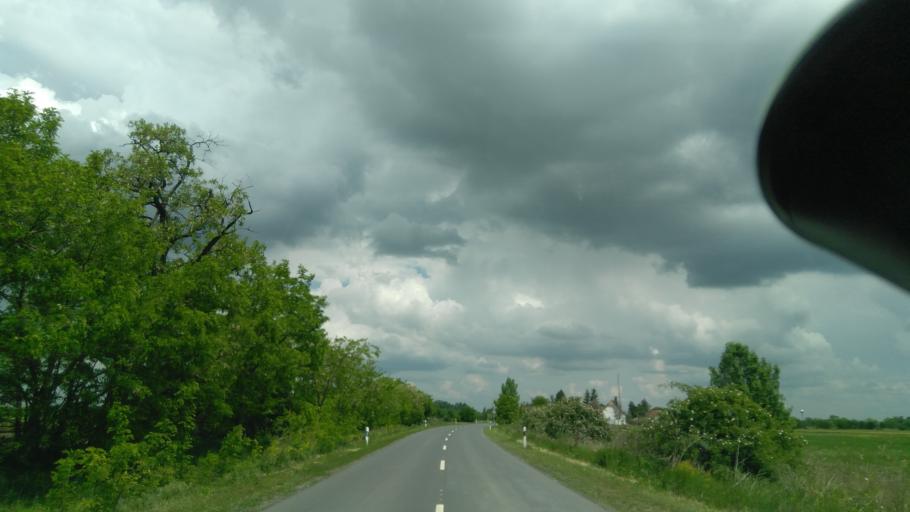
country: HU
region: Bekes
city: Devavanya
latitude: 47.0202
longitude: 20.9351
